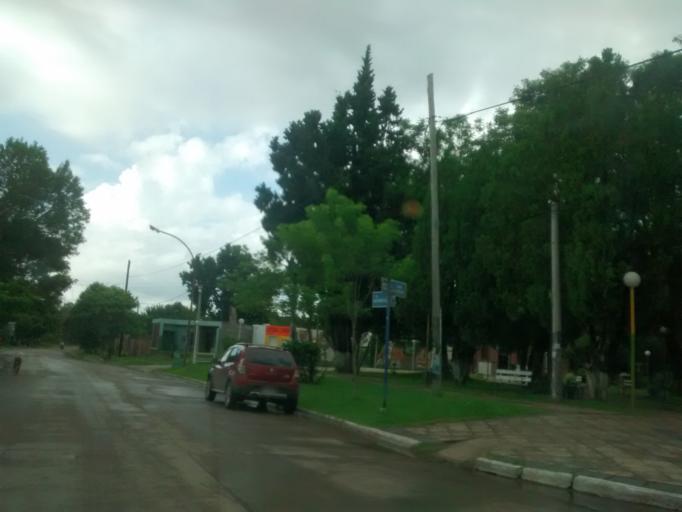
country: AR
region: Chaco
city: Puerto Tirol
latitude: -27.3748
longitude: -59.0869
